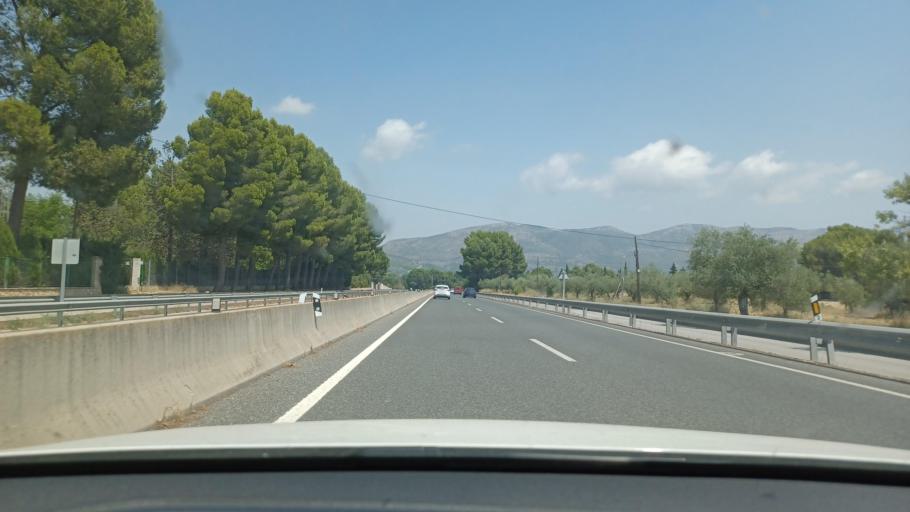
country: ES
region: Valencia
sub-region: Provincia de Alicante
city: Muro del Alcoy
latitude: 38.7679
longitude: -0.4448
